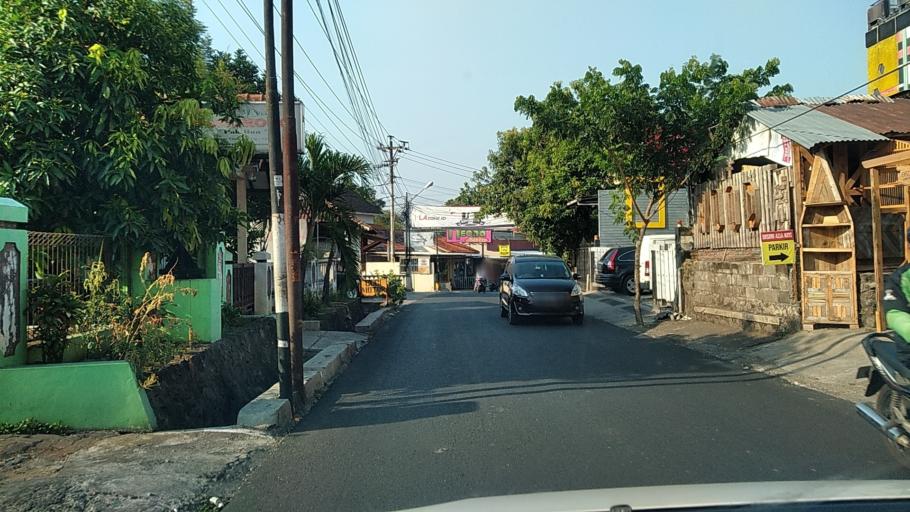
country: ID
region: Central Java
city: Semarang
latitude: -7.0663
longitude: 110.4273
